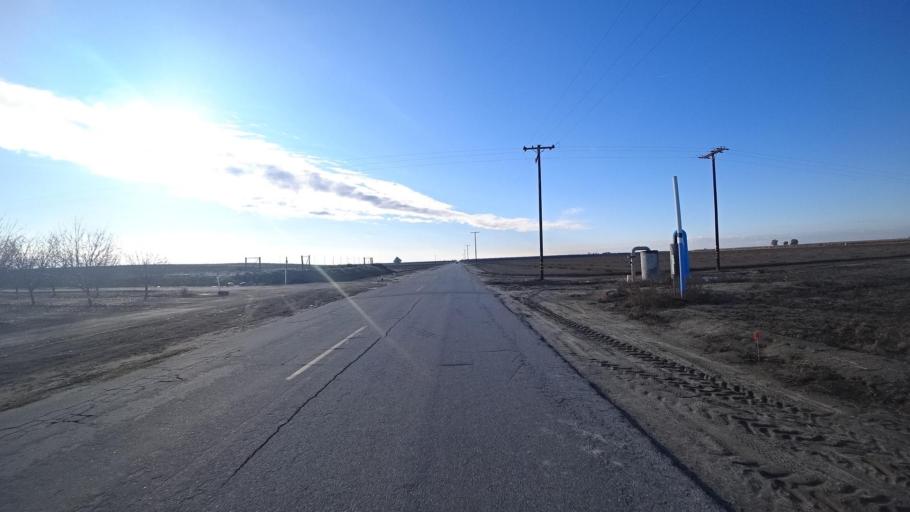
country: US
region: California
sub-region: Kern County
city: Delano
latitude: 35.7543
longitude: -119.3299
